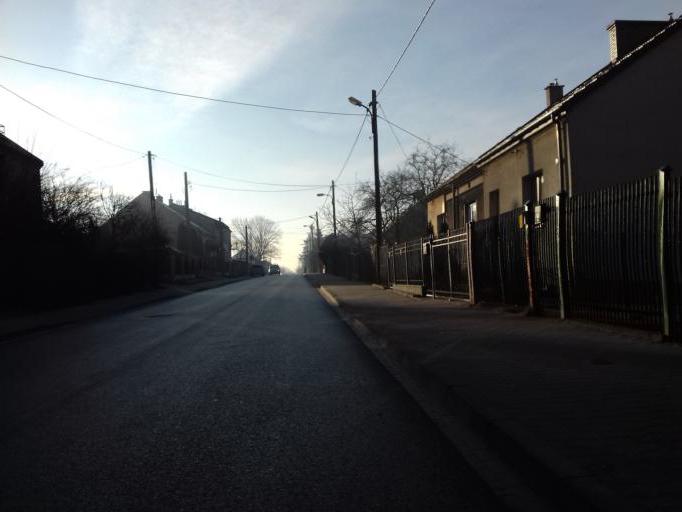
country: PL
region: Lesser Poland Voivodeship
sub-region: Krakow
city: Krakow
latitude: 50.0229
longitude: 19.9424
